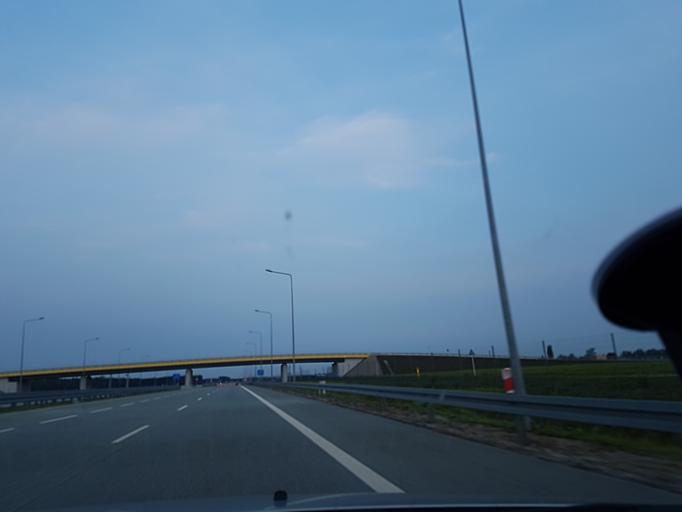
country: PL
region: Lodz Voivodeship
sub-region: Powiat lodzki wschodni
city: Tuszyn
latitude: 51.6421
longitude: 19.5468
